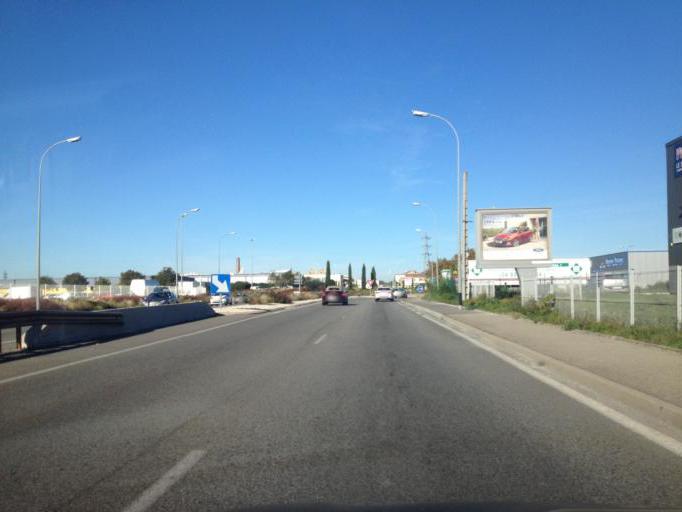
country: FR
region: Provence-Alpes-Cote d'Azur
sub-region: Departement du Vaucluse
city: Le Pontet
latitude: 43.9813
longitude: 4.8592
